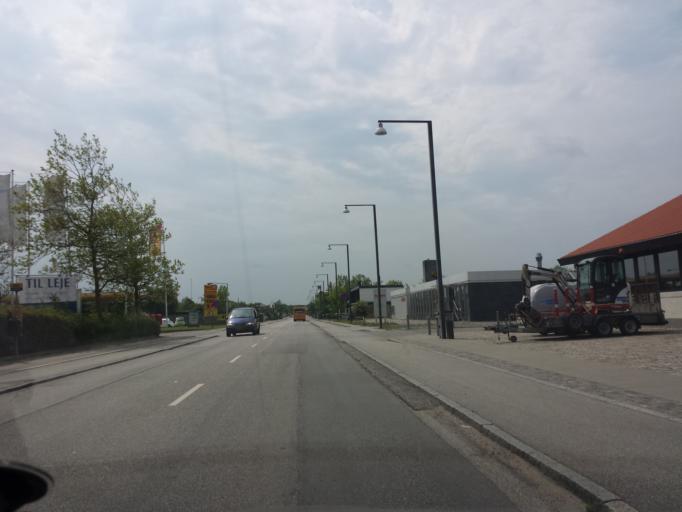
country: DK
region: Capital Region
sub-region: Herlev Kommune
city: Herlev
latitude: 55.7005
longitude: 12.4322
